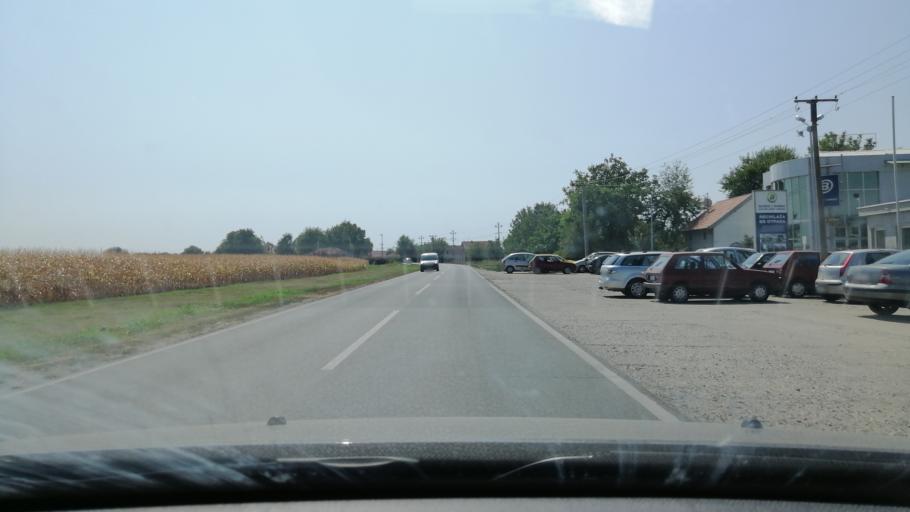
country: RS
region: Central Serbia
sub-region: Belgrade
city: Grocka
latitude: 44.7767
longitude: 20.7245
